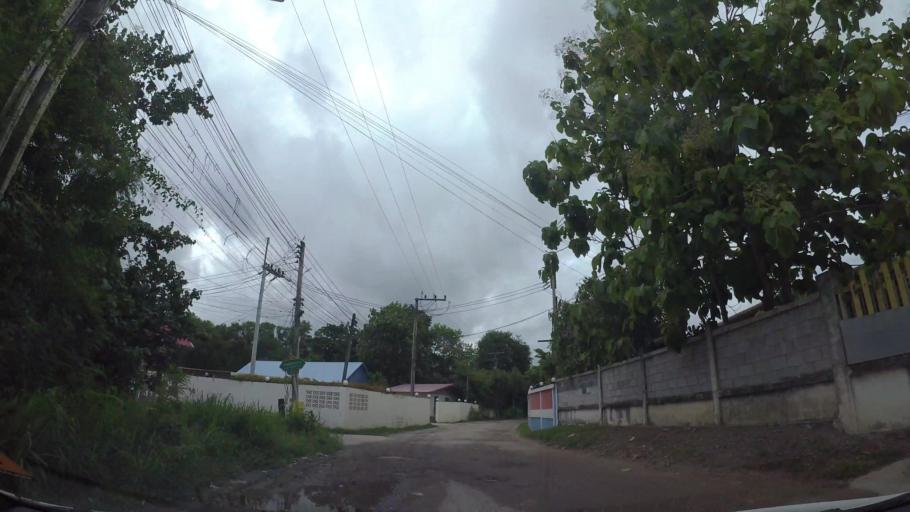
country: TH
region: Rayong
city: Rayong
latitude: 12.6675
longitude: 101.2583
